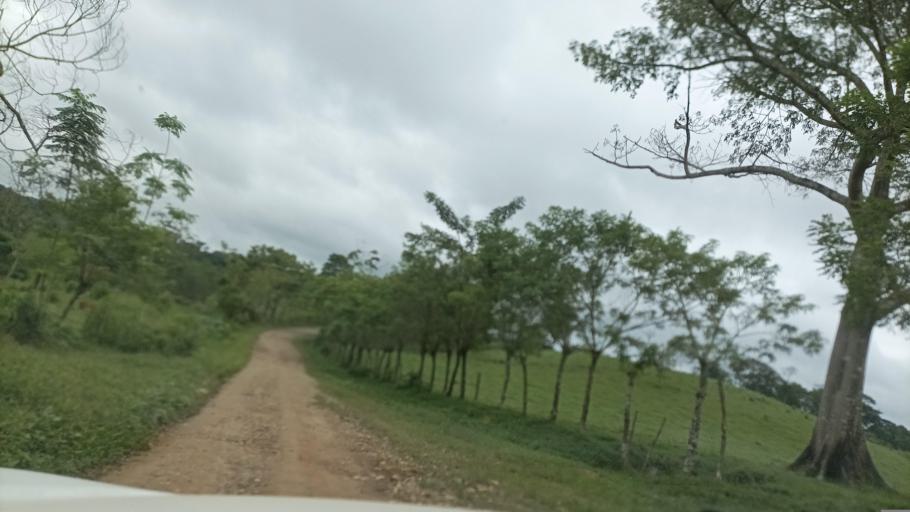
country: MX
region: Veracruz
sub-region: Uxpanapa
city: Poblado 10
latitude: 17.4446
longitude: -94.4028
